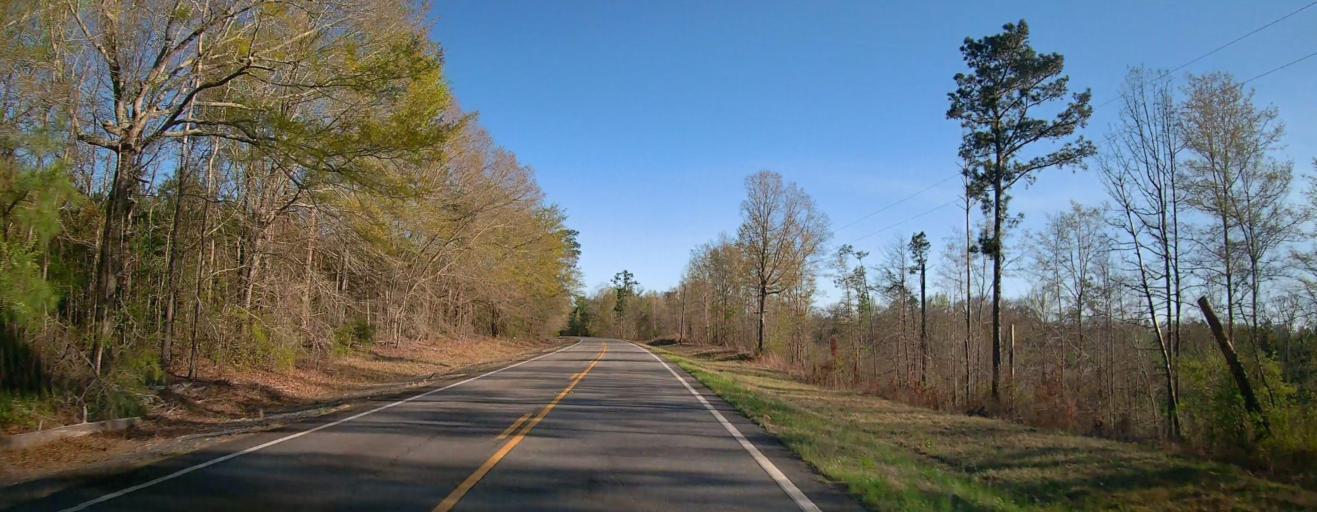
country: US
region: Georgia
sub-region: Baldwin County
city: Hardwick
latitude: 32.9517
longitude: -83.1655
